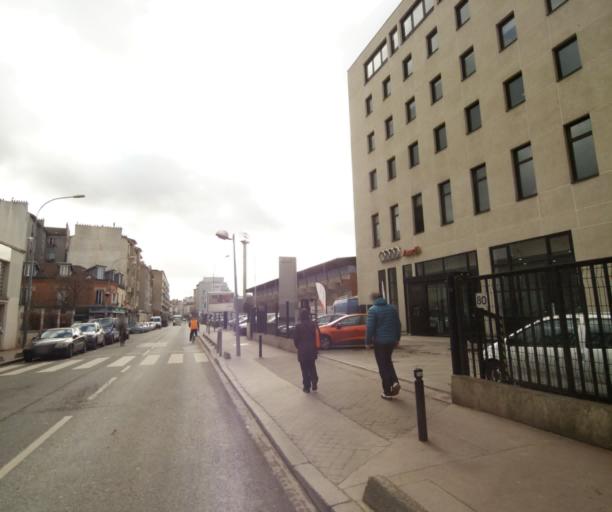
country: FR
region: Ile-de-France
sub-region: Paris
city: Saint-Ouen
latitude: 48.9074
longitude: 2.3413
